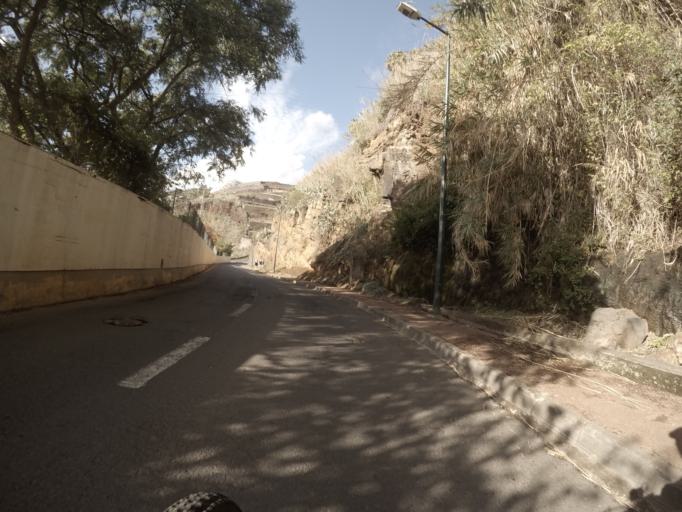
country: PT
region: Madeira
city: Camara de Lobos
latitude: 32.6410
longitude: -16.9507
